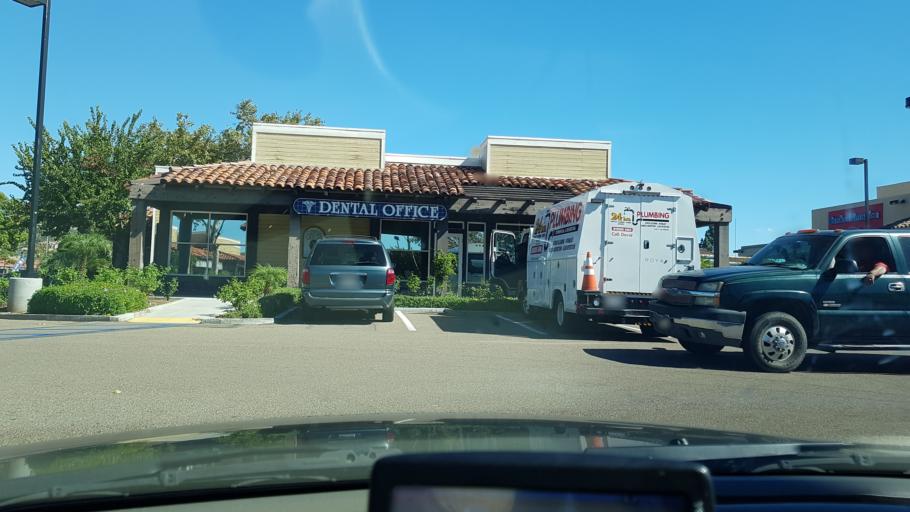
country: US
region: California
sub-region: San Diego County
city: Fairbanks Ranch
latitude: 32.9180
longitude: -117.1258
